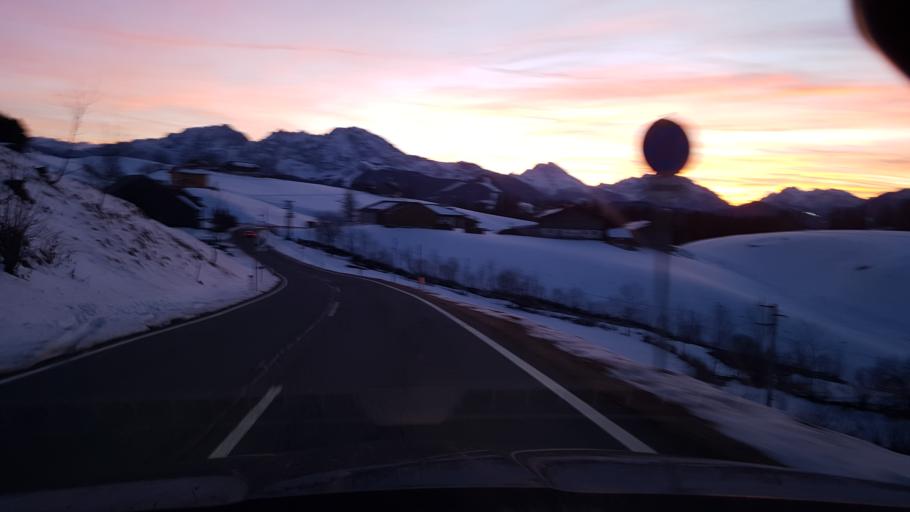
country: AT
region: Salzburg
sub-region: Politischer Bezirk Hallein
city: Krispl
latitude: 47.7136
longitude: 13.1742
